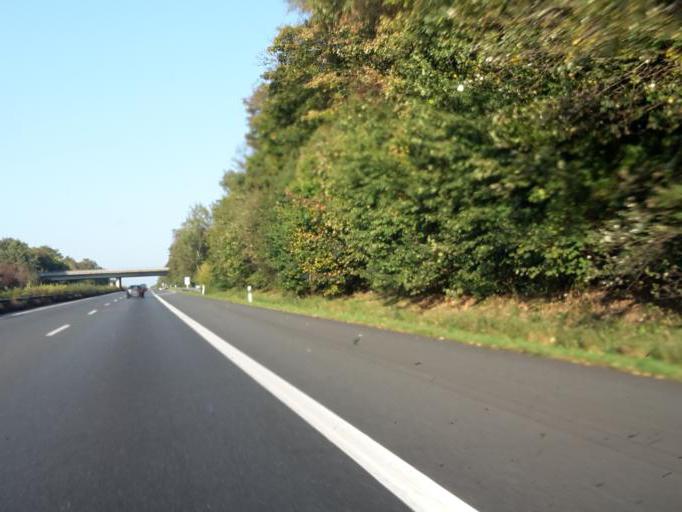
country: DE
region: Lower Saxony
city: Neuenkirchen
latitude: 52.5056
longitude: 8.0880
